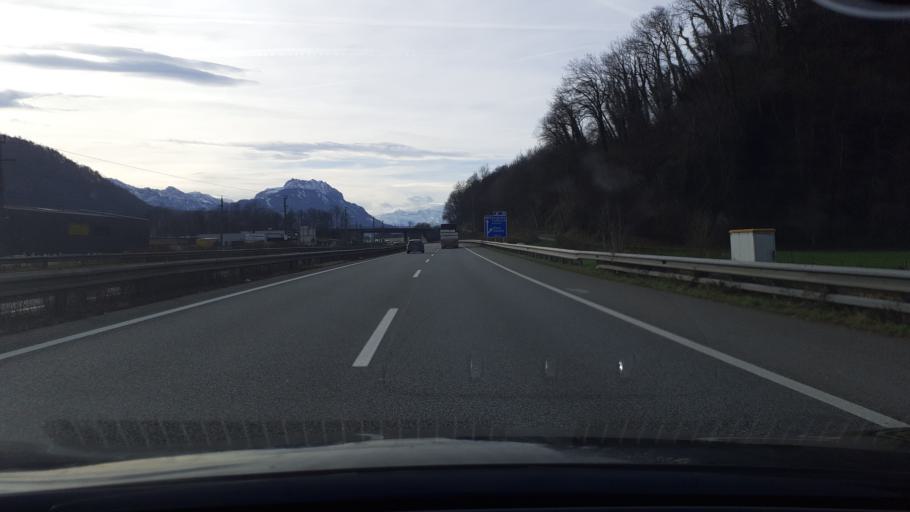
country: AT
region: Vorarlberg
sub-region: Politischer Bezirk Feldkirch
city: Gotzis
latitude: 47.3255
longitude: 9.6266
